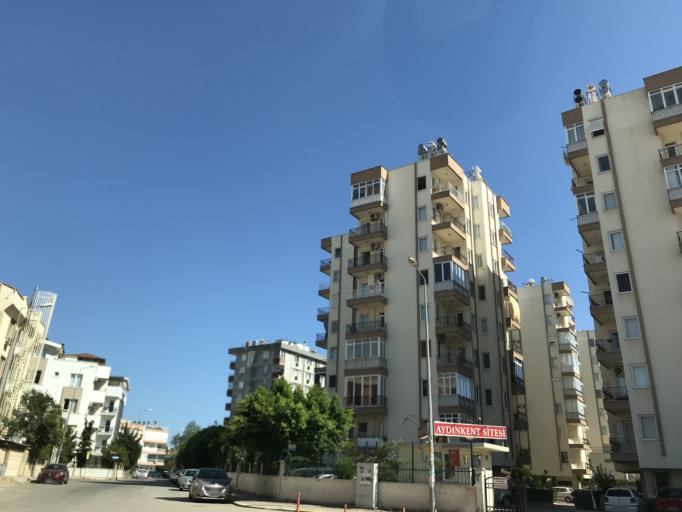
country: TR
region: Antalya
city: Antalya
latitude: 36.9019
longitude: 30.6574
